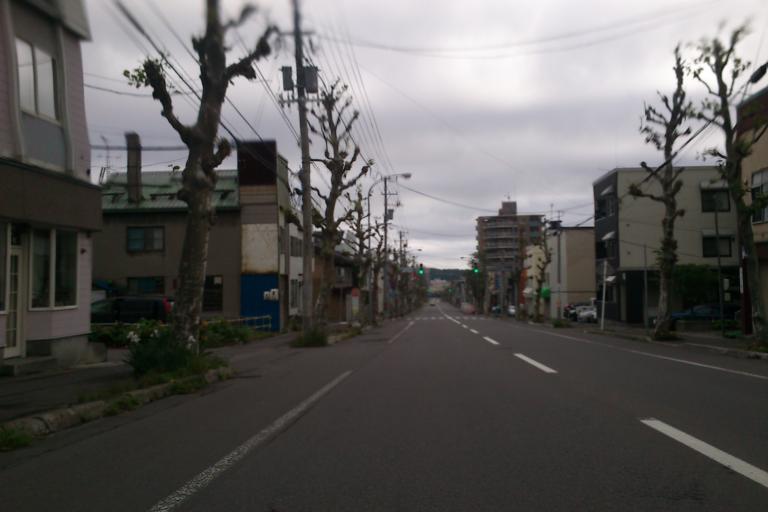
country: JP
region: Hokkaido
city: Otaru
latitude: 43.1877
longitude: 140.9888
